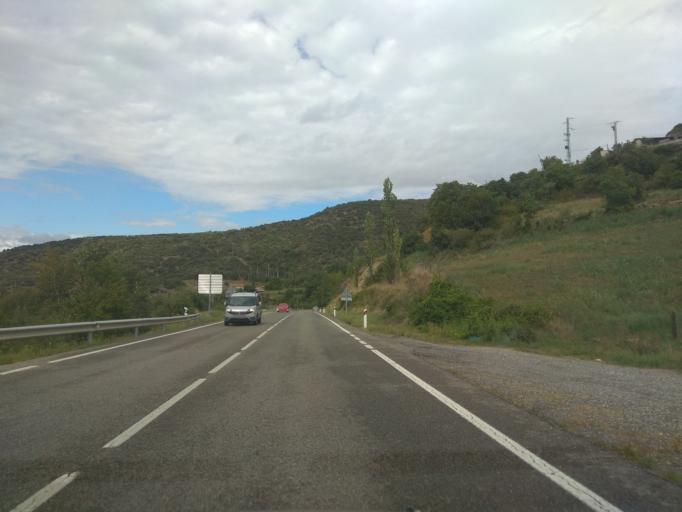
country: ES
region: Catalonia
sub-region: Provincia de Lleida
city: Alas i Cerc
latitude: 42.3580
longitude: 1.5200
